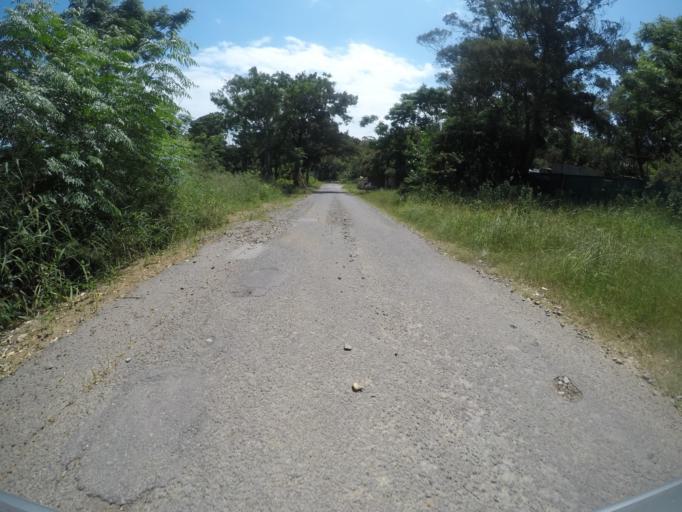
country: ZA
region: Eastern Cape
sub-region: Buffalo City Metropolitan Municipality
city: East London
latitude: -32.9699
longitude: 27.8558
